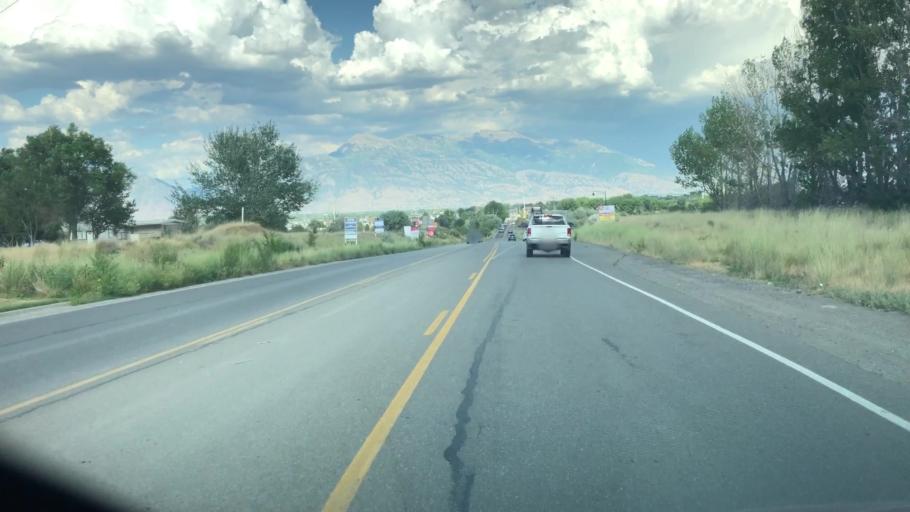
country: US
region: Utah
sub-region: Utah County
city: Saratoga Springs
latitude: 40.3874
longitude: -111.9090
